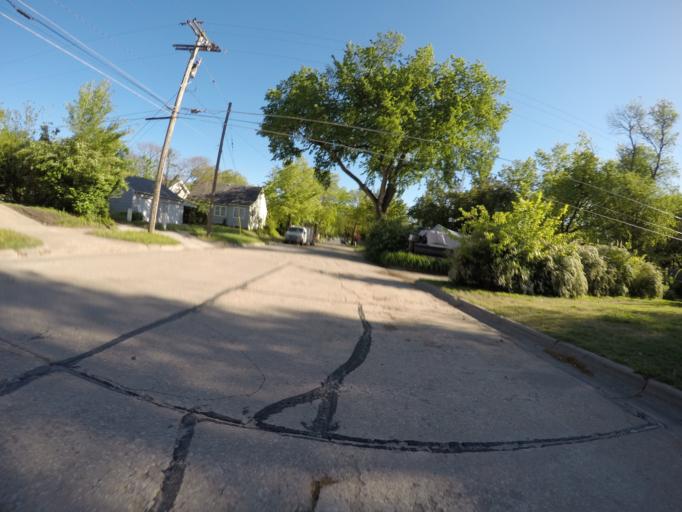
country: US
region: Kansas
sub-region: Riley County
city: Manhattan
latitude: 39.1915
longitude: -96.5683
